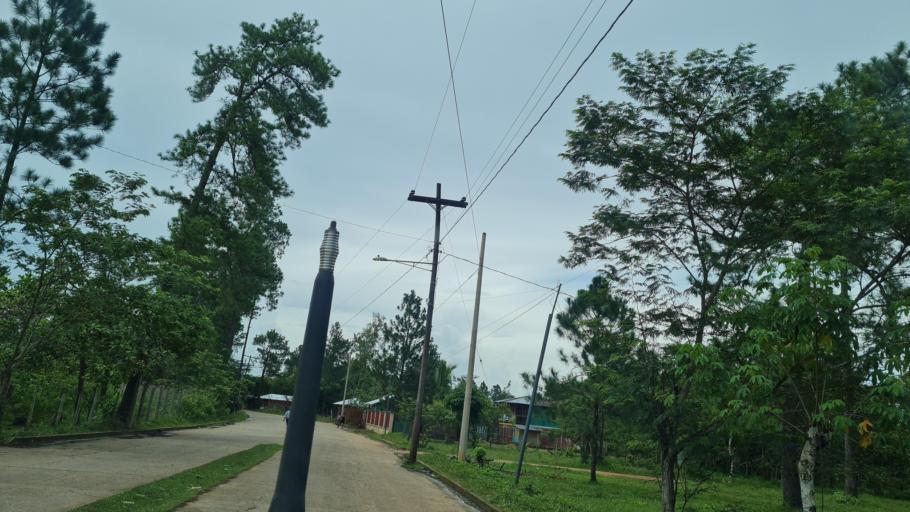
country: NI
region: Atlantico Norte (RAAN)
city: Waspam
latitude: 14.7280
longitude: -83.9702
